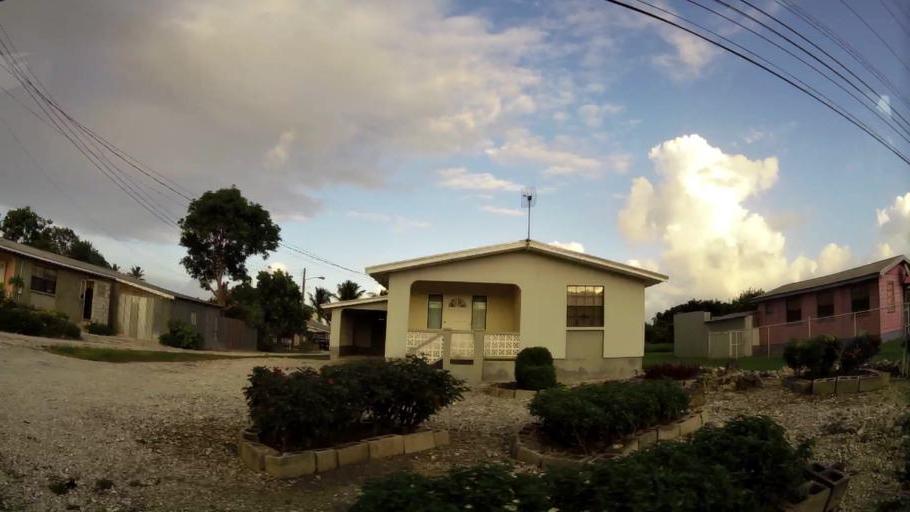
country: BB
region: Saint Philip
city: Crane
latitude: 13.1058
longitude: -59.4684
